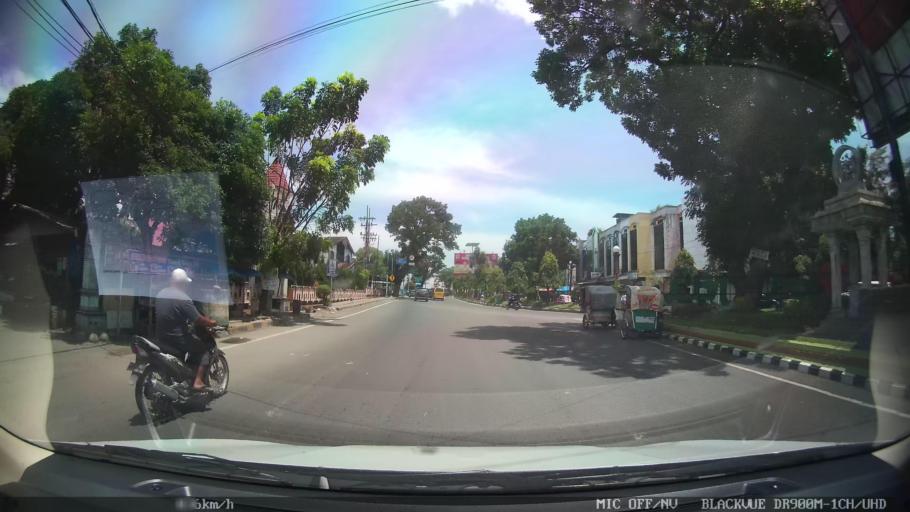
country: ID
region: North Sumatra
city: Binjai
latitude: 3.6071
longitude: 98.4951
